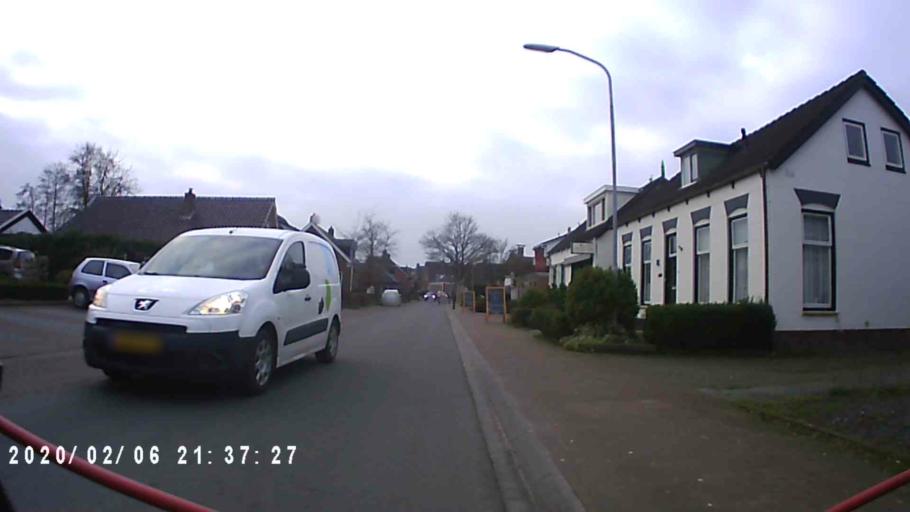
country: NL
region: Groningen
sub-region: Gemeente Zuidhorn
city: Noordhorn
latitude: 53.2637
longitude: 6.3945
